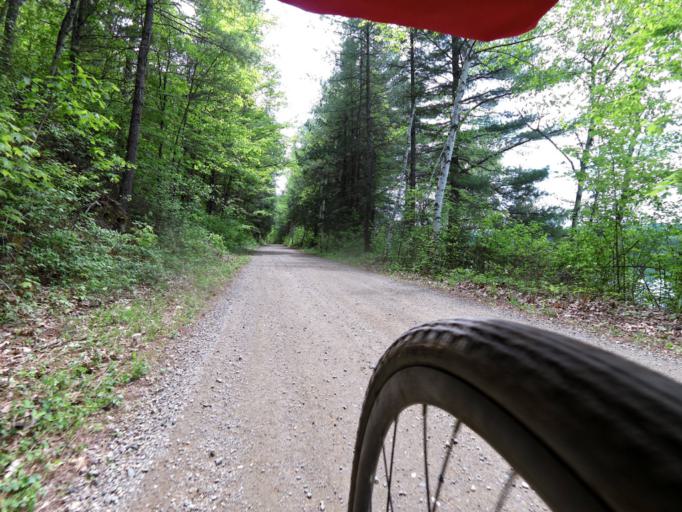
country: CA
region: Ontario
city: Renfrew
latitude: 45.1943
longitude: -76.6854
